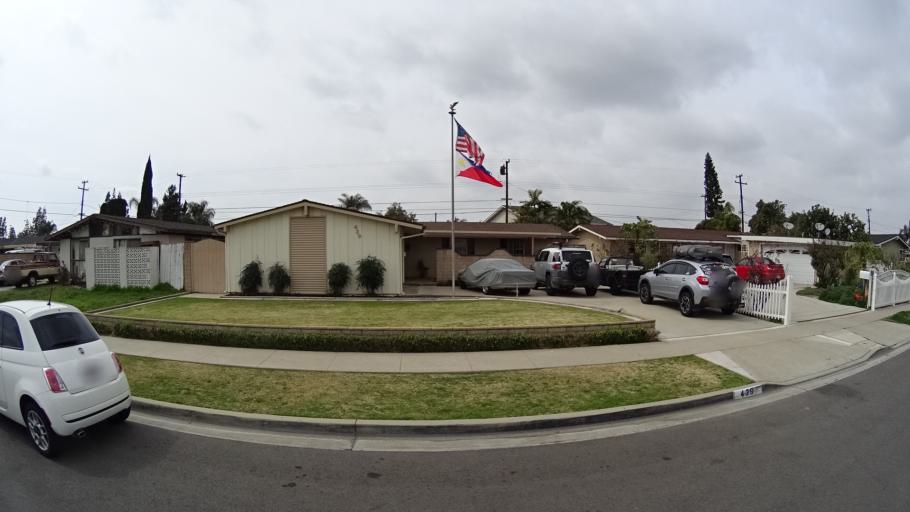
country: US
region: California
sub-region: Orange County
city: Stanton
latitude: 33.8257
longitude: -117.9896
